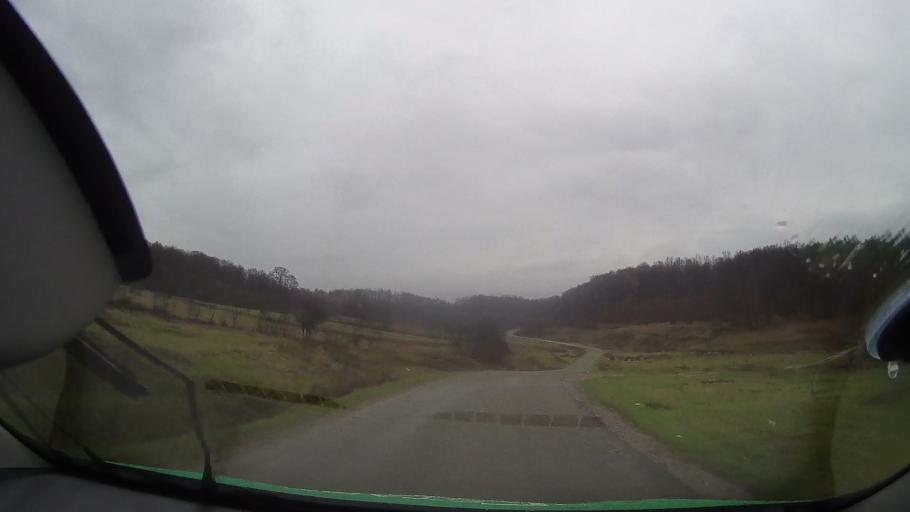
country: RO
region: Bihor
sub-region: Comuna Rabagani
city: Rabagani
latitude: 46.7202
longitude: 22.2317
